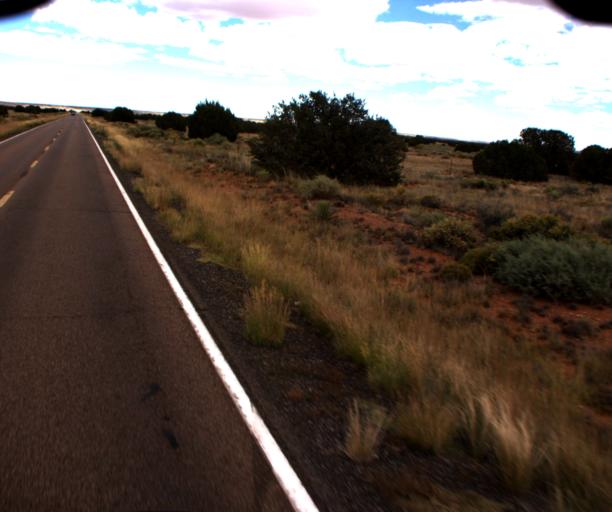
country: US
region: Arizona
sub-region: Navajo County
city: Heber-Overgaard
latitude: 34.5795
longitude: -110.4062
